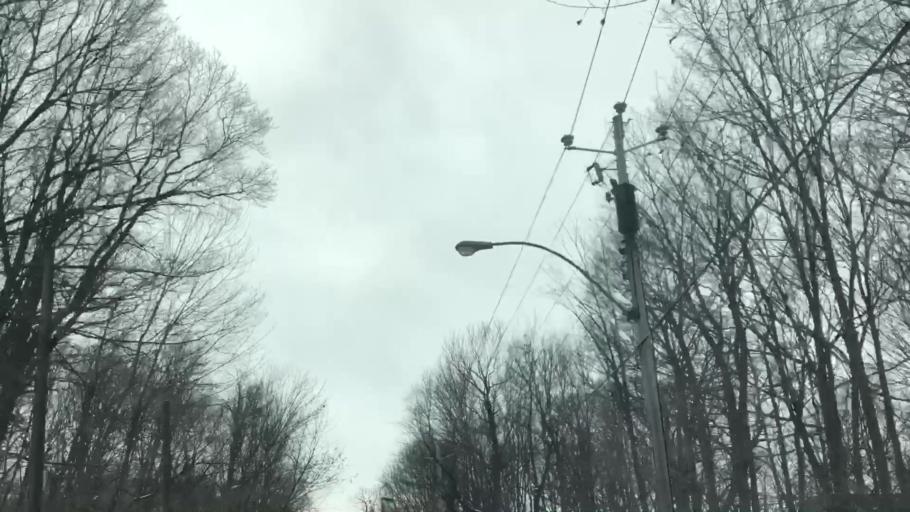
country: CA
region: Quebec
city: Dorval
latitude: 45.5176
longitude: -73.7445
